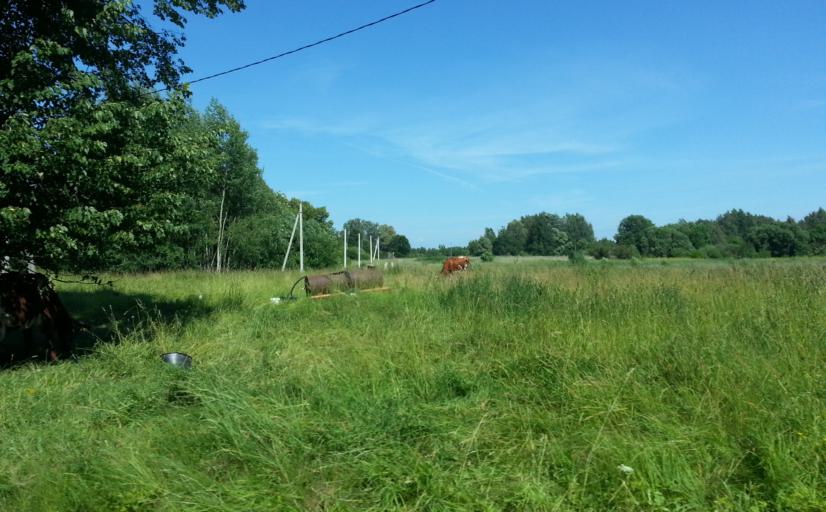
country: LT
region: Panevezys
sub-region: Birzai
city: Birzai
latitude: 56.2389
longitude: 24.6911
